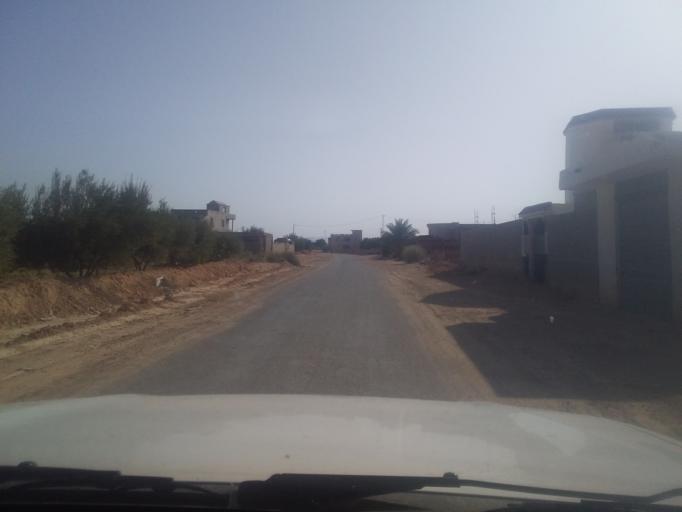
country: TN
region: Qabis
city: Matmata
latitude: 33.6081
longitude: 10.2807
